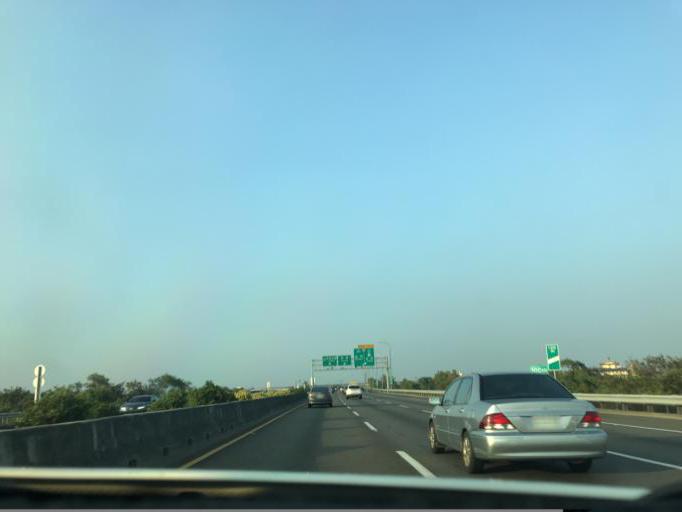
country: TW
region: Taiwan
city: Xinying
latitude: 23.2066
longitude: 120.2368
